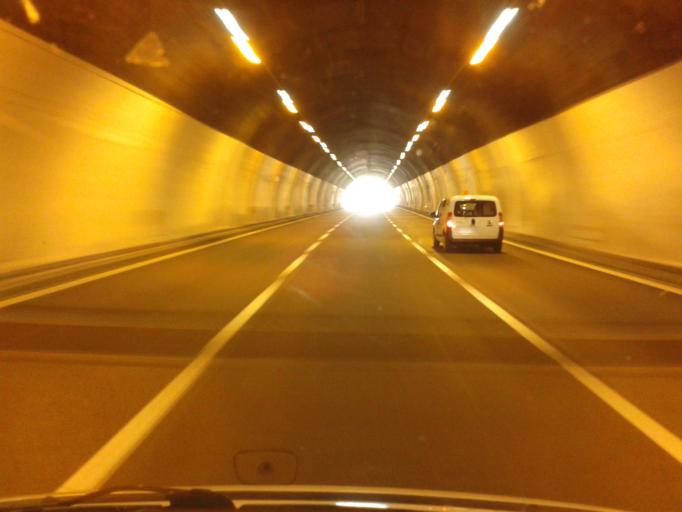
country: IT
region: Liguria
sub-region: Provincia di Genova
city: Rossiglione
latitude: 44.5505
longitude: 8.6709
